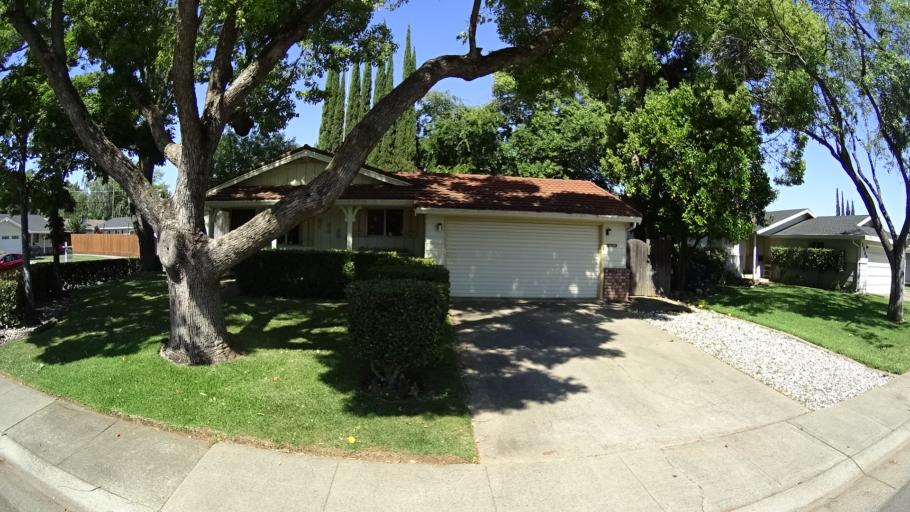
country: US
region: California
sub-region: Sacramento County
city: Rosemont
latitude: 38.5517
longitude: -121.3875
